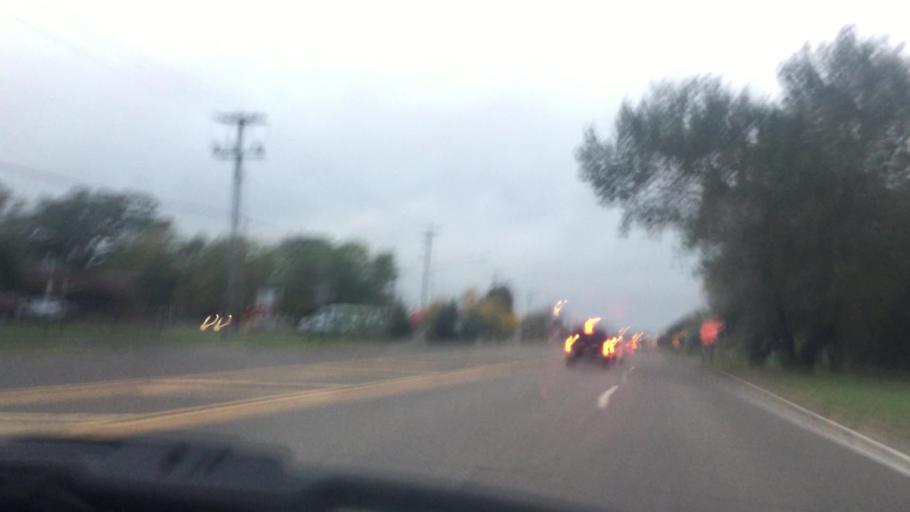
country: US
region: Minnesota
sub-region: Anoka County
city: Spring Lake Park
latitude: 45.1079
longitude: -93.2525
